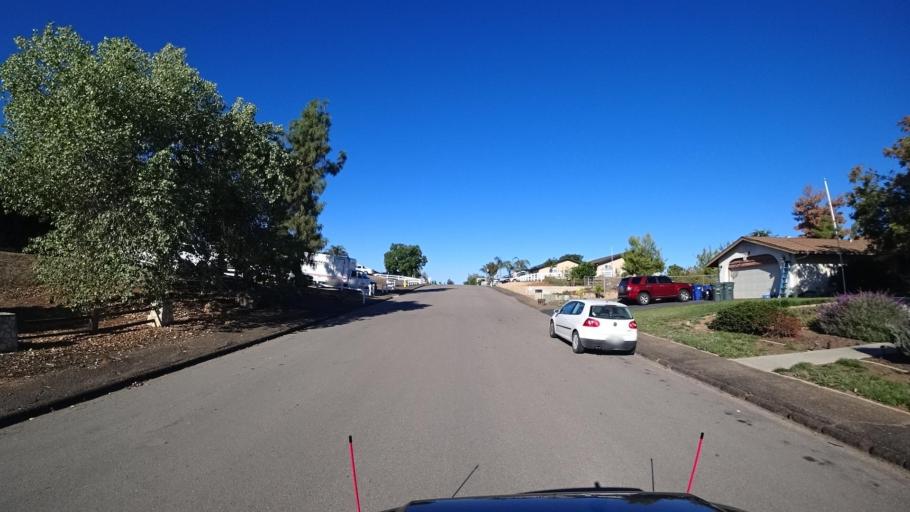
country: US
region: California
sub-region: San Diego County
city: Alpine
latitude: 32.8307
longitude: -116.7565
